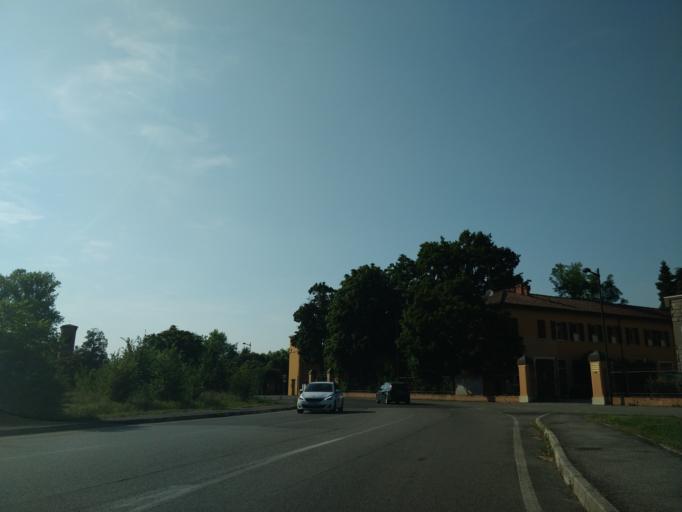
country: IT
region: Emilia-Romagna
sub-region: Provincia di Bologna
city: Progresso
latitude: 44.5588
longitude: 11.3548
